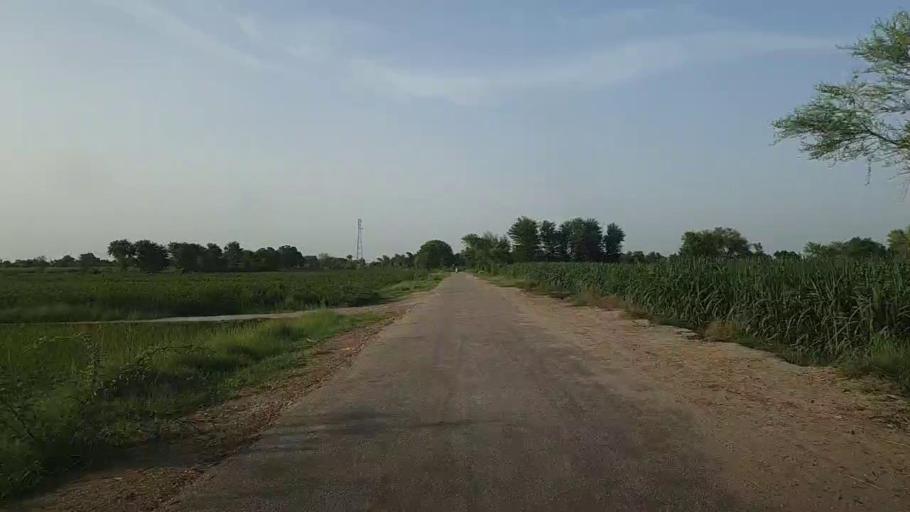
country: PK
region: Sindh
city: Bhiria
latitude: 26.9049
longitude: 68.2634
